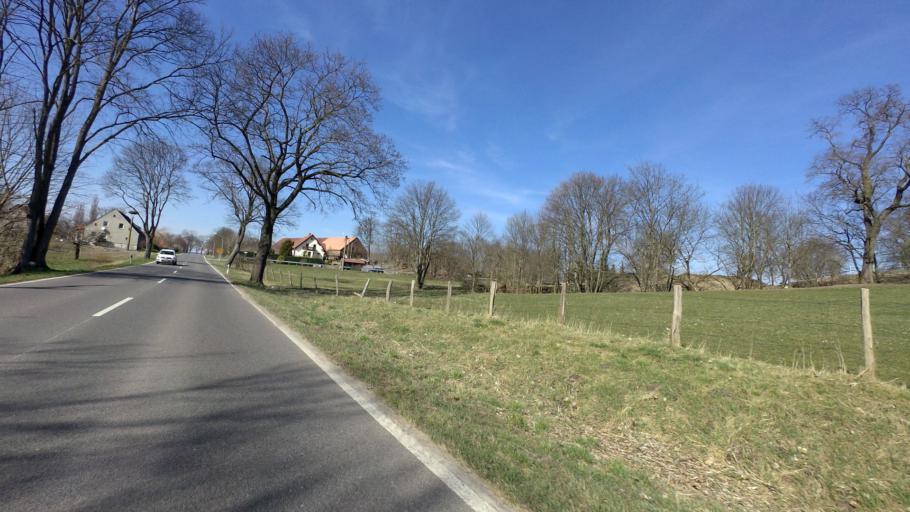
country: DE
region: Brandenburg
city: Protzel
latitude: 52.6287
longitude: 14.0144
